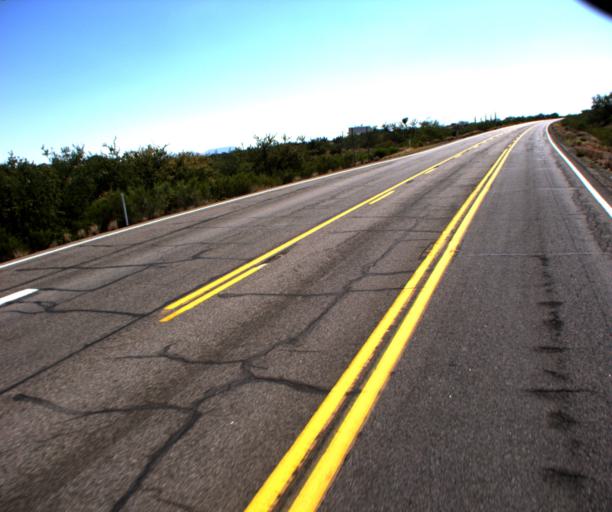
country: US
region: Arizona
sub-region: Pinal County
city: Oracle
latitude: 32.6222
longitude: -110.7948
